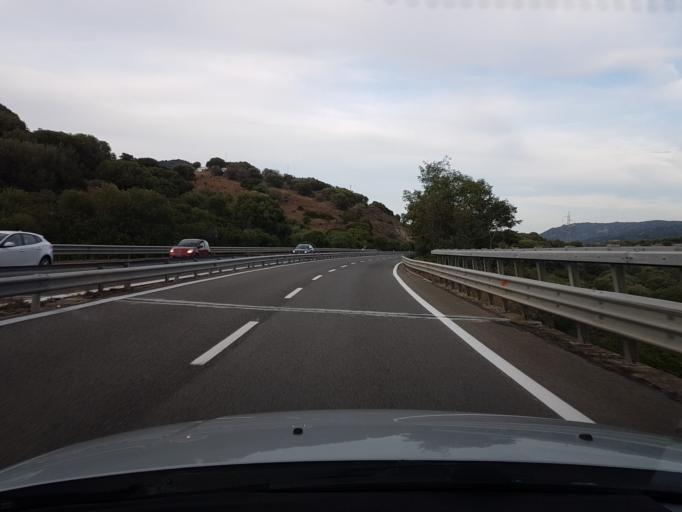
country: IT
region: Sardinia
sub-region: Provincia di Nuoro
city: Orune
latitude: 40.3645
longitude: 9.3645
